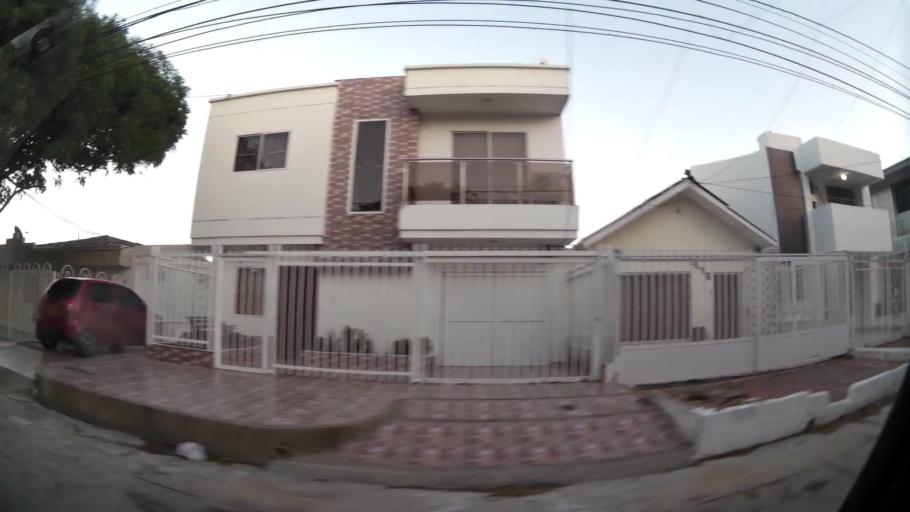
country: CO
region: Atlantico
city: Barranquilla
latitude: 10.9790
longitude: -74.8077
